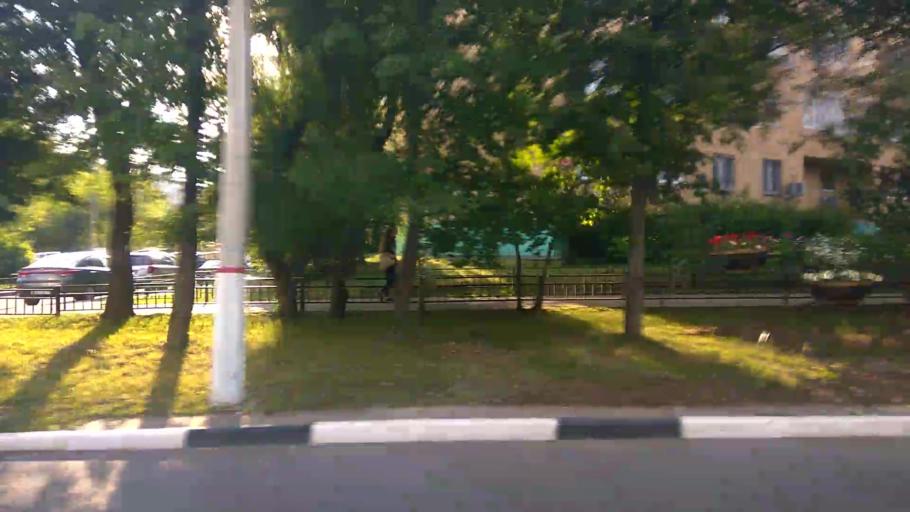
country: RU
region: Moskovskaya
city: Mytishchi
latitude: 55.9046
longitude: 37.7156
